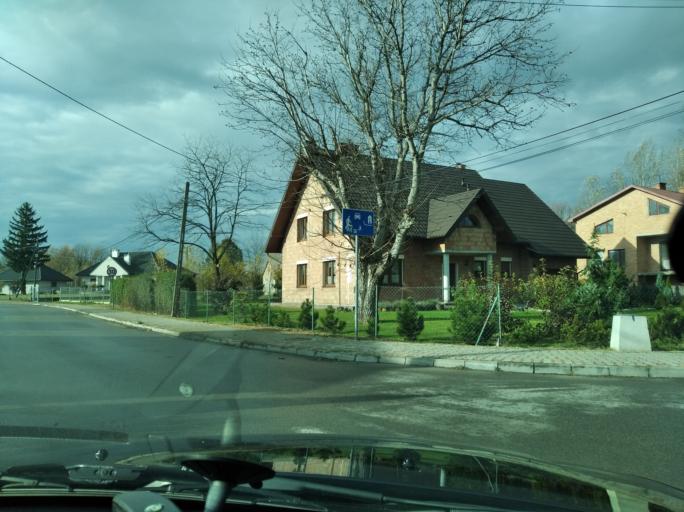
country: PL
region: Subcarpathian Voivodeship
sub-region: Powiat debicki
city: Brzeznica
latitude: 50.0830
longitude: 21.5215
